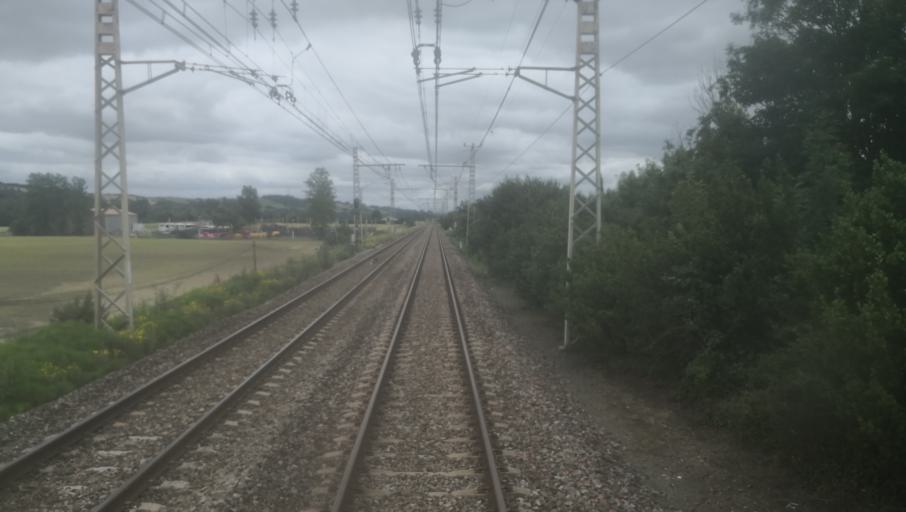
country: FR
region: Midi-Pyrenees
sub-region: Departement de la Haute-Garonne
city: Avignonet-Lauragais
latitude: 43.3647
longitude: 1.7844
